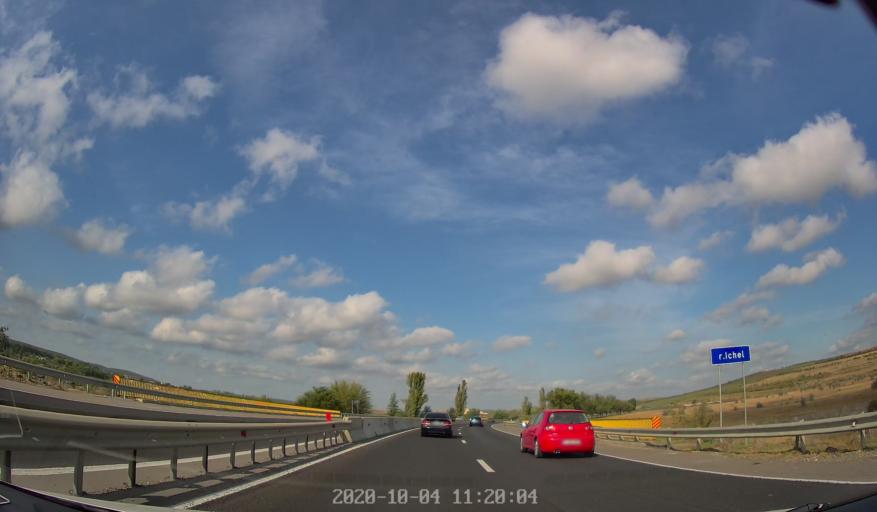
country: MD
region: Chisinau
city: Cricova
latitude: 47.1728
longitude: 28.8010
